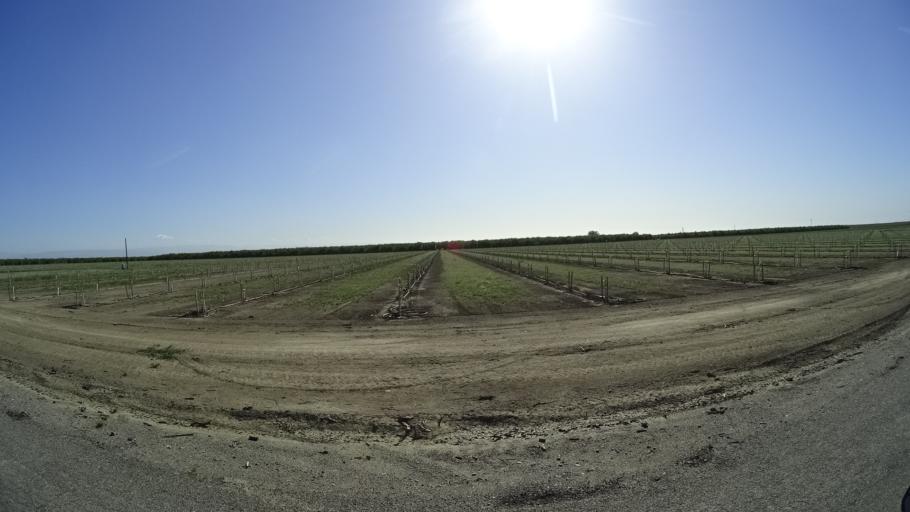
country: US
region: California
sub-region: Glenn County
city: Hamilton City
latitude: 39.6847
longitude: -122.0638
